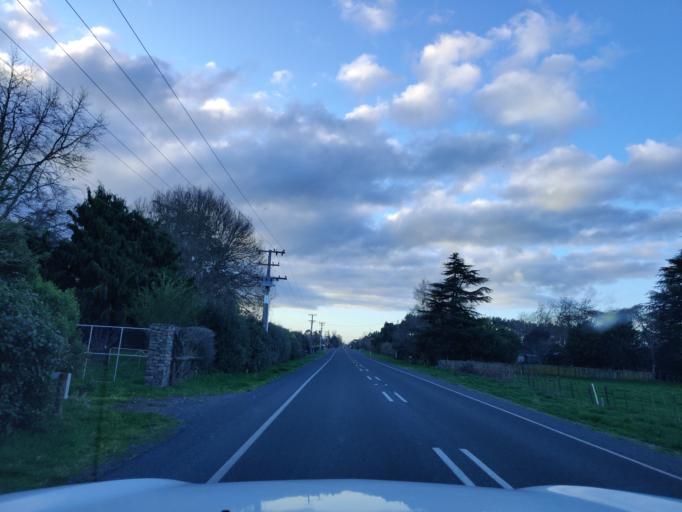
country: NZ
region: Waikato
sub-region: Waipa District
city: Cambridge
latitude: -37.8638
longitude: 175.4390
